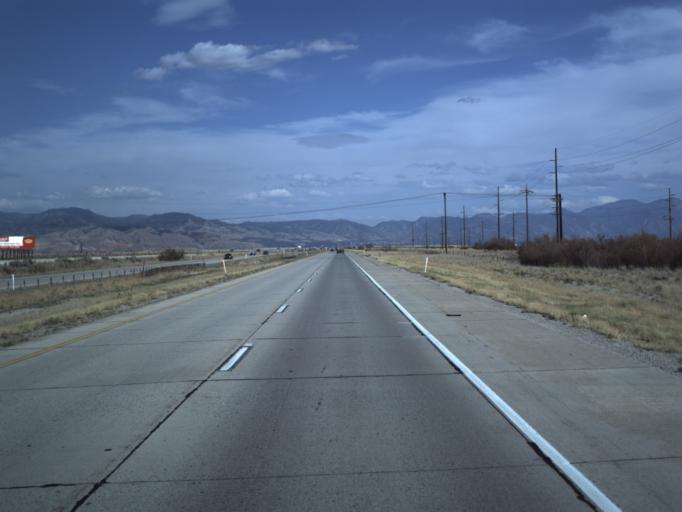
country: US
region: Utah
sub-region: Salt Lake County
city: Magna
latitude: 40.7708
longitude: -112.1027
